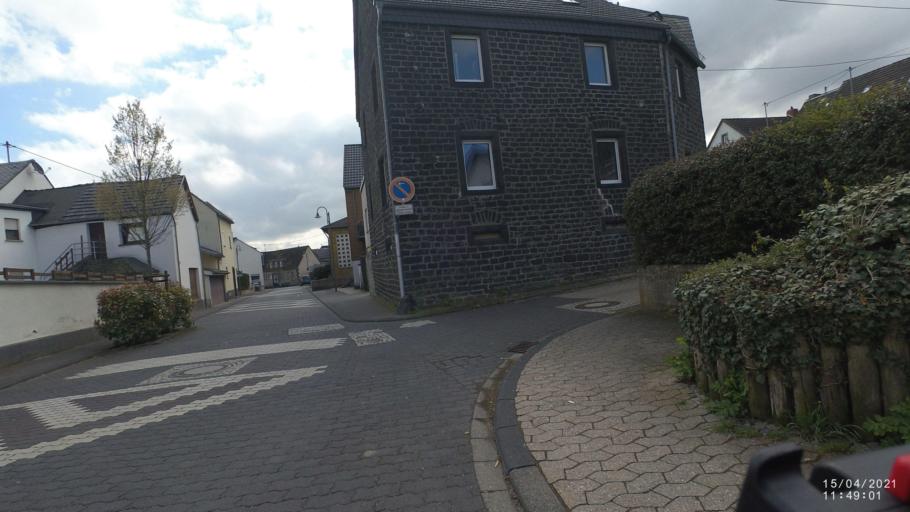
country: DE
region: Rheinland-Pfalz
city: Mendig
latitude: 50.3711
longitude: 7.2773
